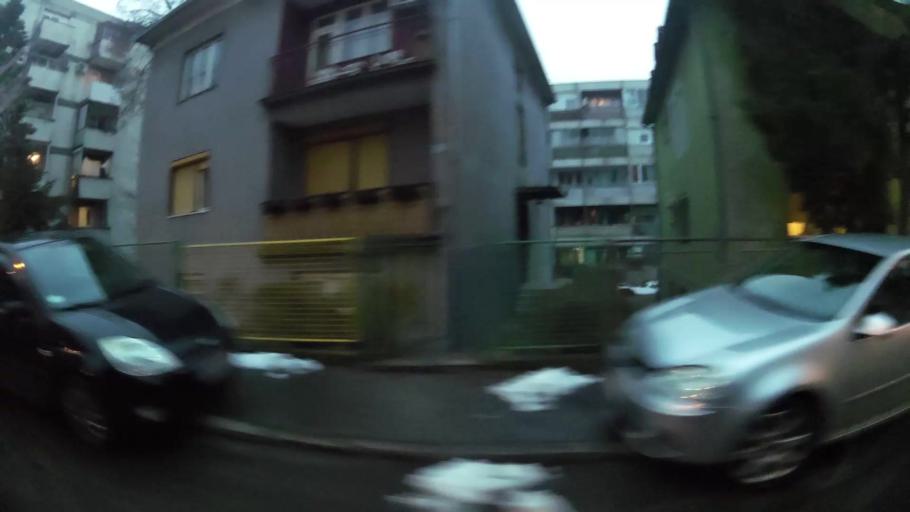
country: RS
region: Central Serbia
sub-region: Belgrade
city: Vozdovac
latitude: 44.7775
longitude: 20.4850
